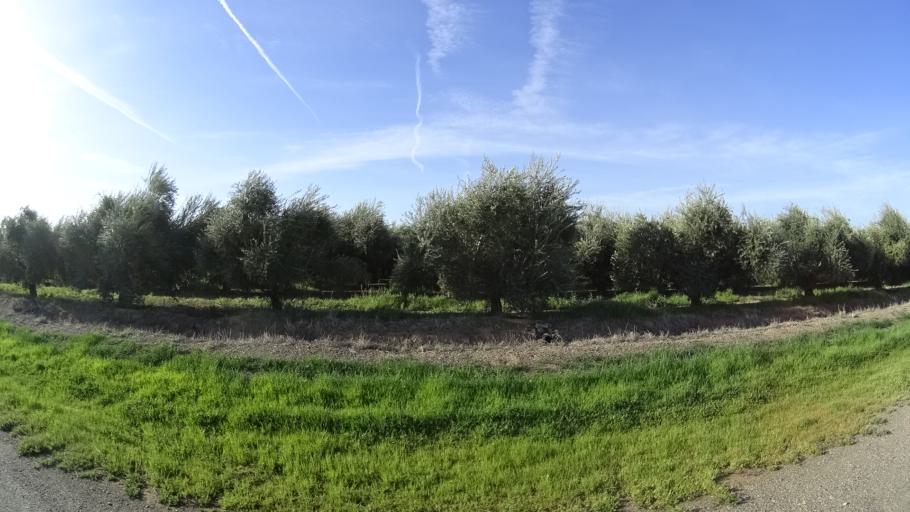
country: US
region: California
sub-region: Glenn County
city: Orland
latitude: 39.7332
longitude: -122.2213
